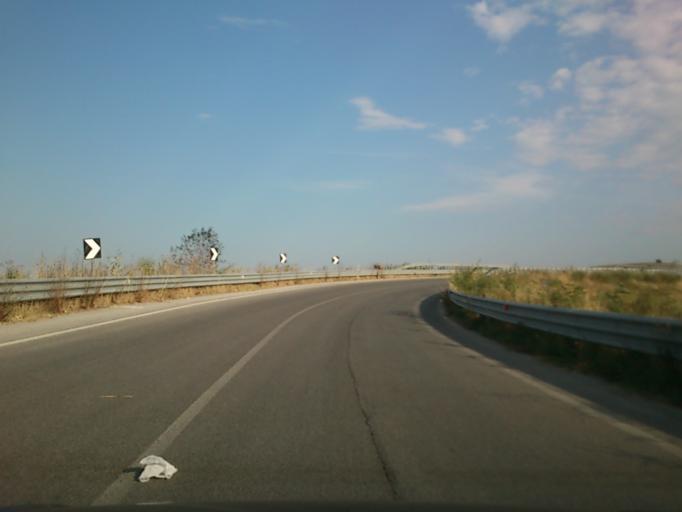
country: IT
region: The Marches
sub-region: Provincia di Pesaro e Urbino
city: Marotta
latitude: 43.8087
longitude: 13.0565
